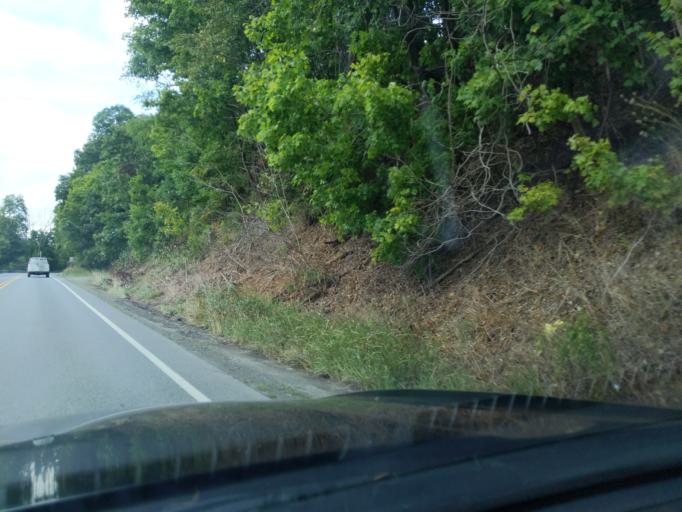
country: US
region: Pennsylvania
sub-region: Blair County
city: Duncansville
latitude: 40.3837
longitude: -78.4138
